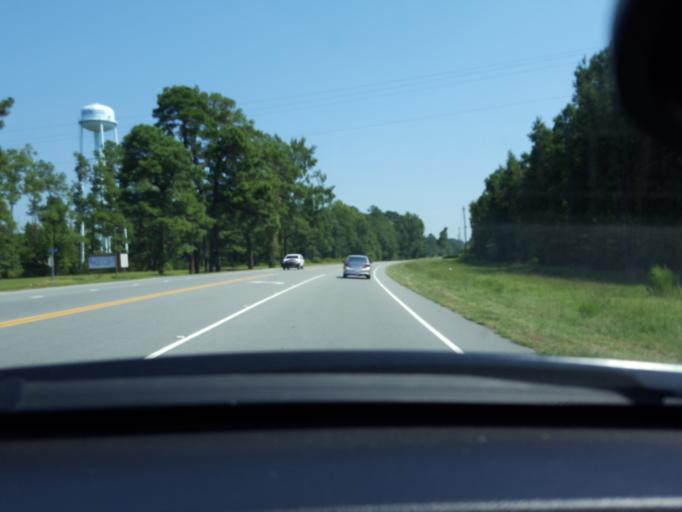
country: US
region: North Carolina
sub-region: Bladen County
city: Elizabethtown
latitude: 34.6536
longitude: -78.5177
